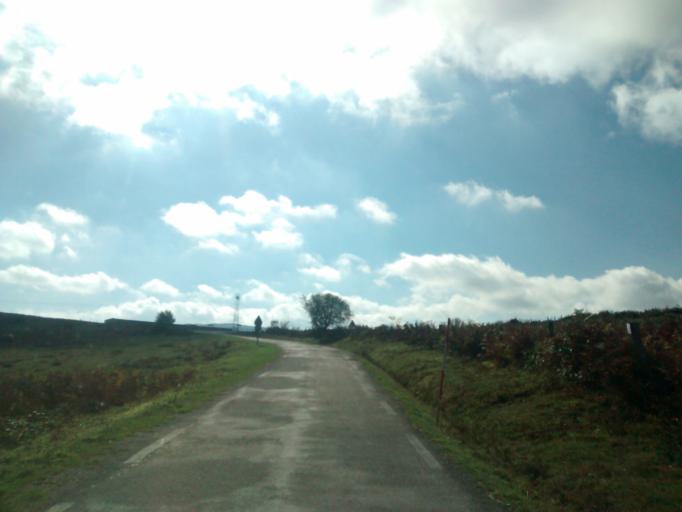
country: ES
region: Castille and Leon
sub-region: Provincia de Burgos
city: Arija
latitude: 42.9254
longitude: -4.0114
